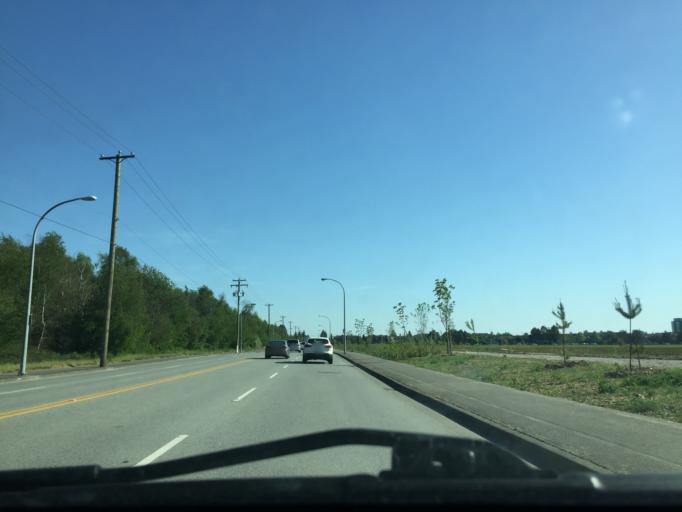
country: CA
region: British Columbia
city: Richmond
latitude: 49.1751
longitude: -123.1141
